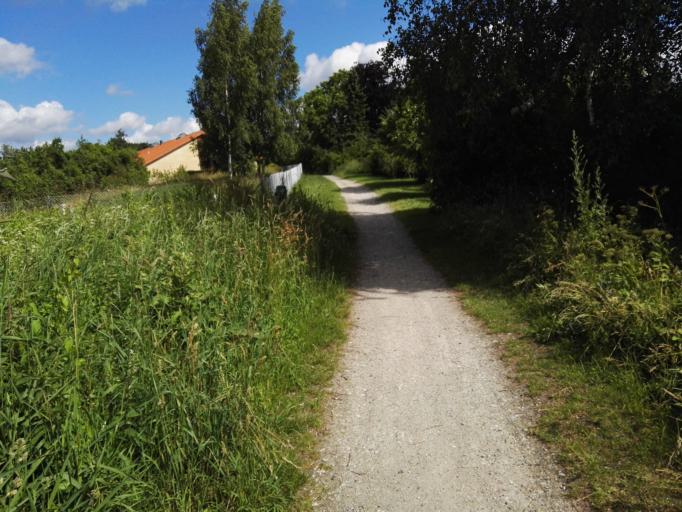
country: DK
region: Capital Region
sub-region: Herlev Kommune
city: Herlev
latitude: 55.7343
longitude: 12.4094
